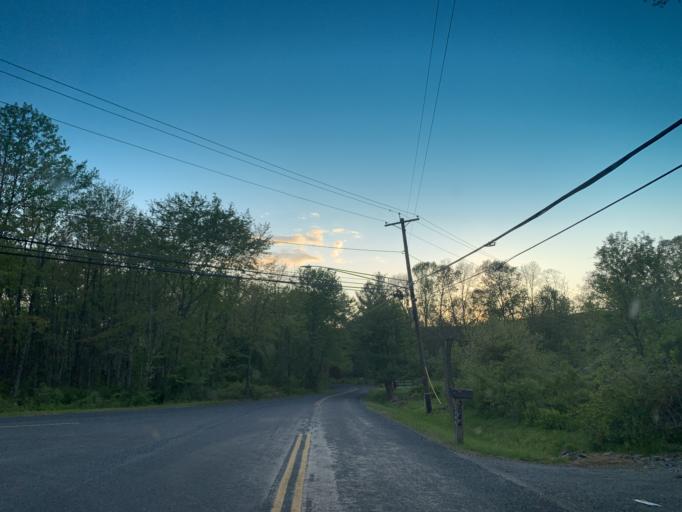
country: US
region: Maryland
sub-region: Harford County
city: Riverside
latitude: 39.5251
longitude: -76.2507
